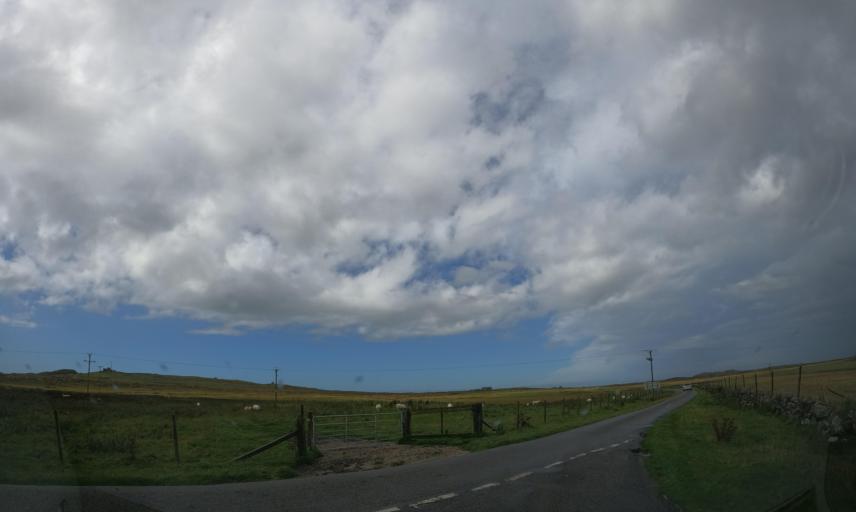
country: GB
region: Scotland
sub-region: Eilean Siar
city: Barra
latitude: 56.5132
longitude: -6.8169
